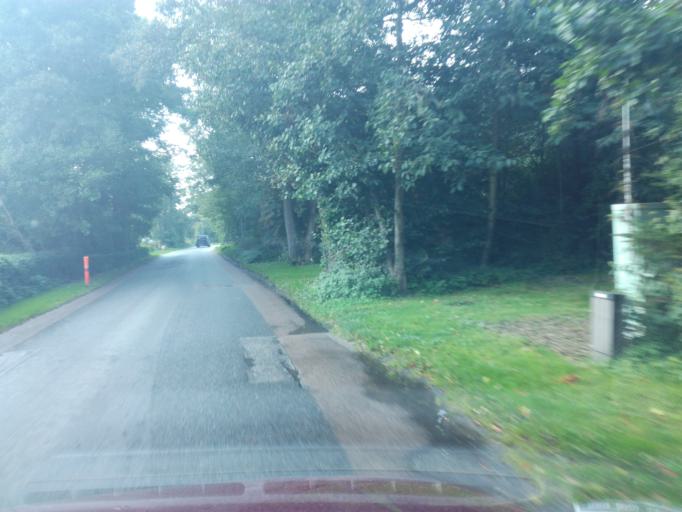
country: DK
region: South Denmark
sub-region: Fredericia Kommune
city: Fredericia
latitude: 55.6255
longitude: 9.8041
